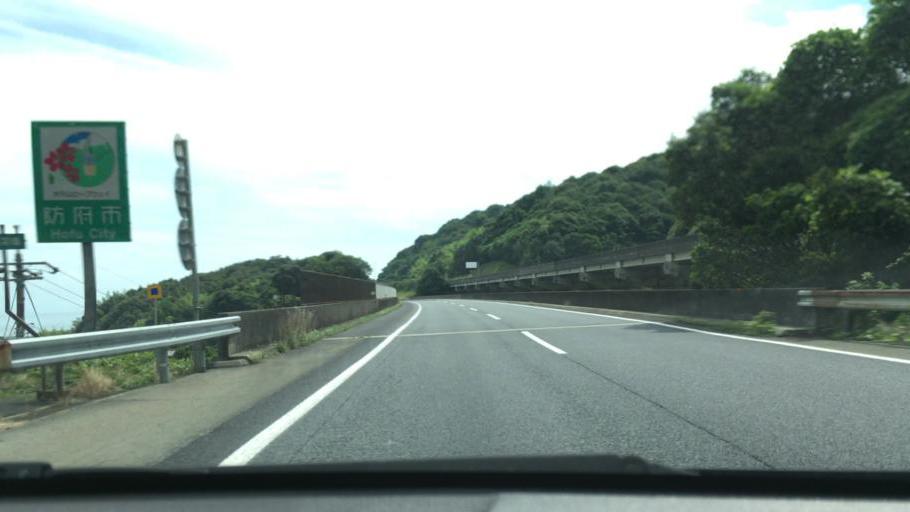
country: JP
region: Yamaguchi
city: Hofu
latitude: 34.0687
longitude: 131.6593
